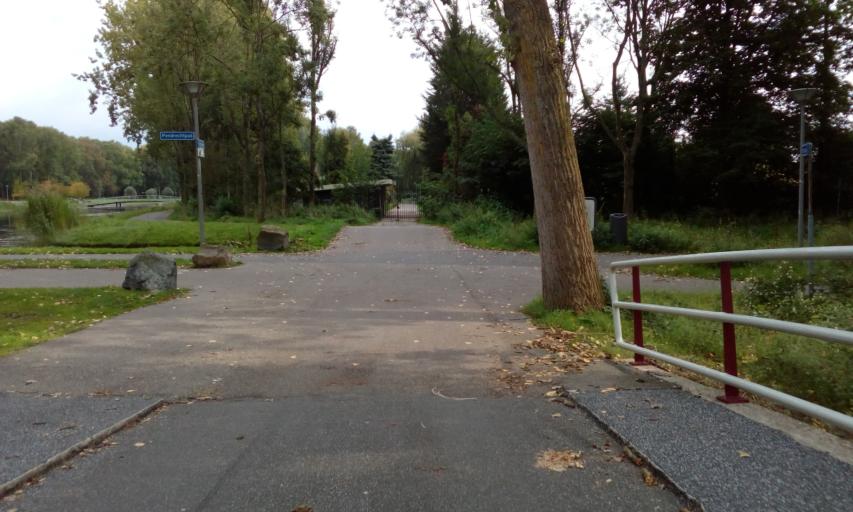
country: NL
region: South Holland
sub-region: Gemeente Rotterdam
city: Delfshaven
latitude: 51.8831
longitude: 4.4748
